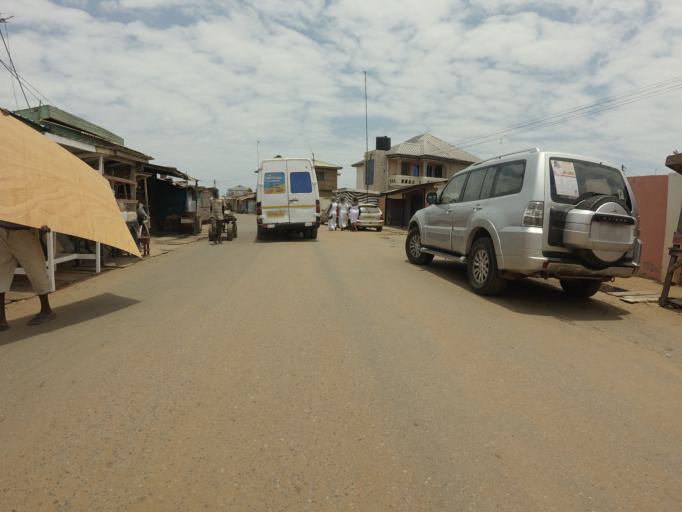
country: GH
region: Greater Accra
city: Nungua
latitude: 5.6006
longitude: -0.0835
